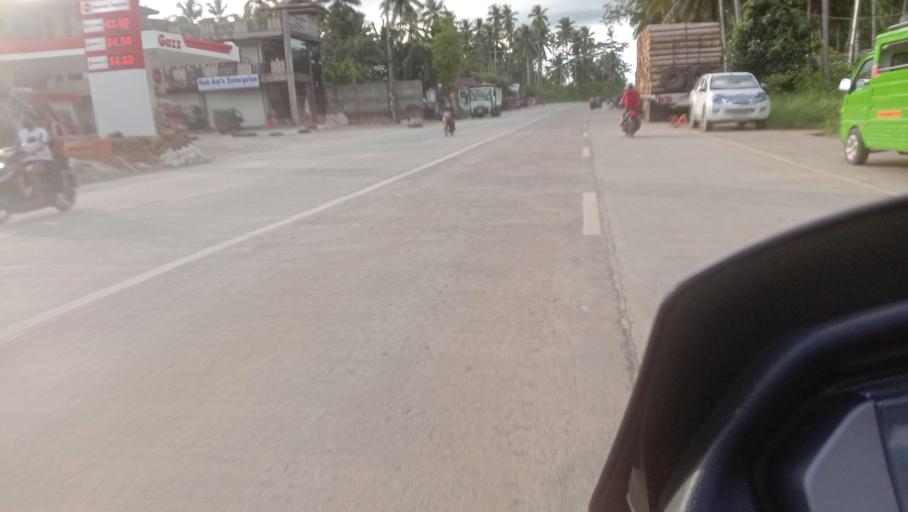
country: PH
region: Caraga
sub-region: Province of Surigao del Sur
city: Barobo
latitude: 8.5212
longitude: 126.1209
